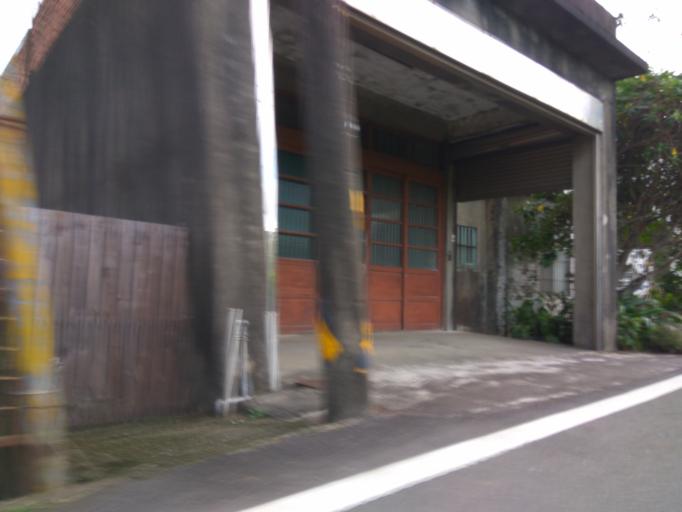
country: TW
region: Taiwan
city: Daxi
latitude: 24.9231
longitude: 121.1924
